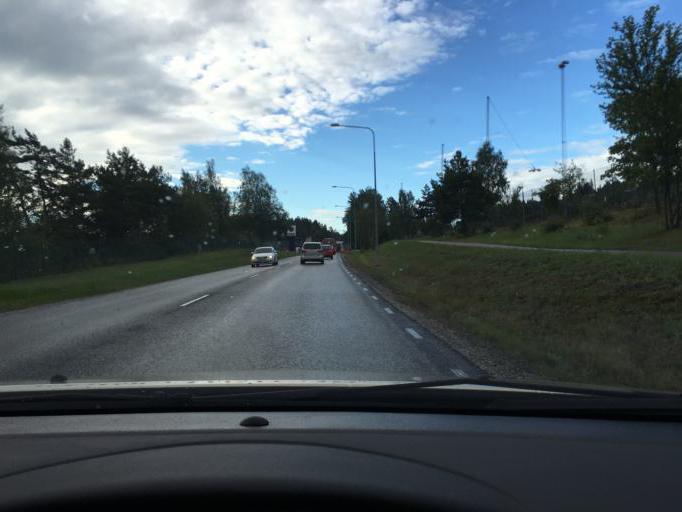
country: SE
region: Stockholm
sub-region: Sodertalje Kommun
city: Pershagen
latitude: 59.1679
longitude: 17.6390
